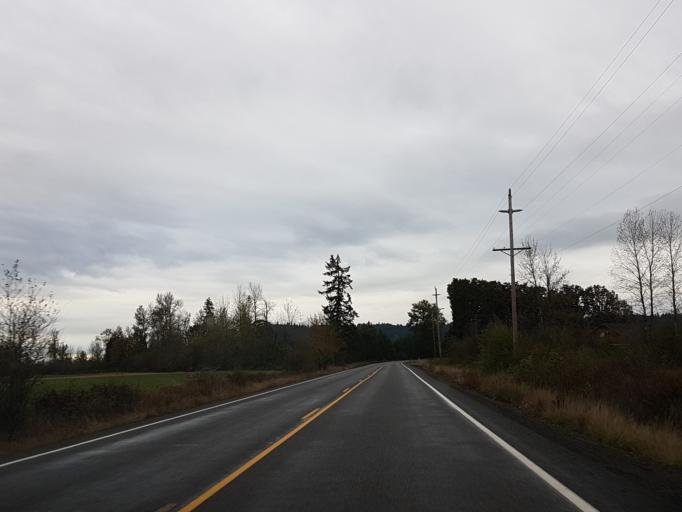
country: US
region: Oregon
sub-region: Marion County
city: Stayton
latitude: 44.7080
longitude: -122.7929
